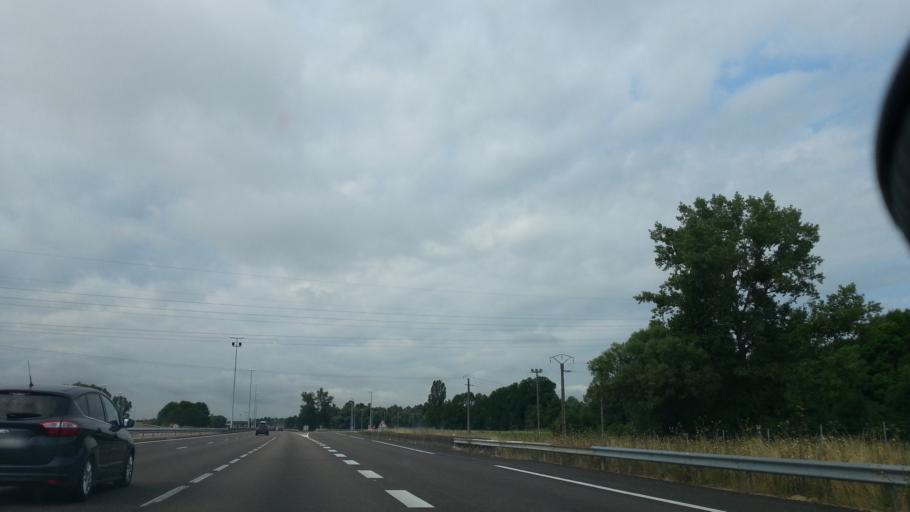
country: FR
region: Bourgogne
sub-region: Departement de la Cote-d'Or
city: Beaune
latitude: 47.0367
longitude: 4.8818
